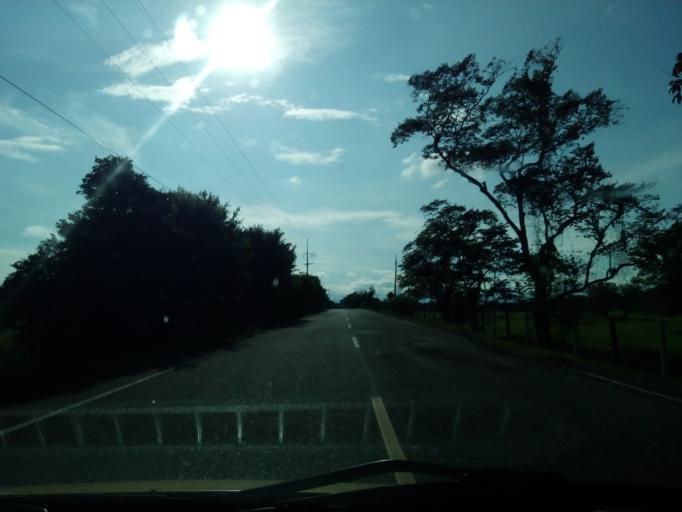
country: CO
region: Boyaca
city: Puerto Boyaca
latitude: 5.9404
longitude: -74.5626
